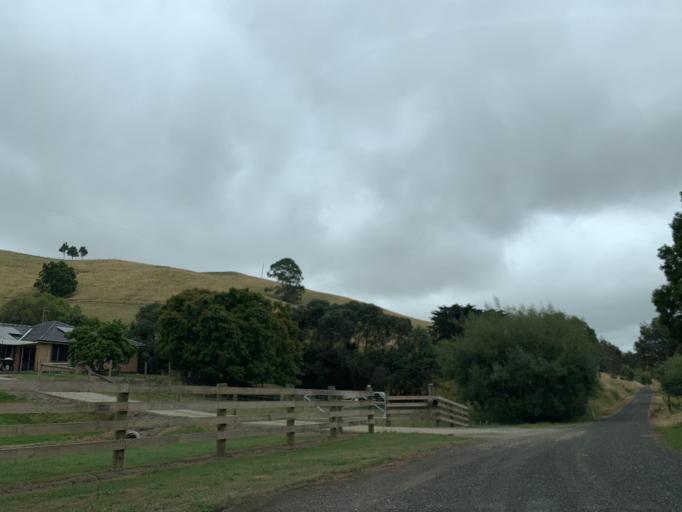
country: AU
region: Victoria
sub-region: Baw Baw
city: Warragul
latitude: -38.3313
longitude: 145.8510
